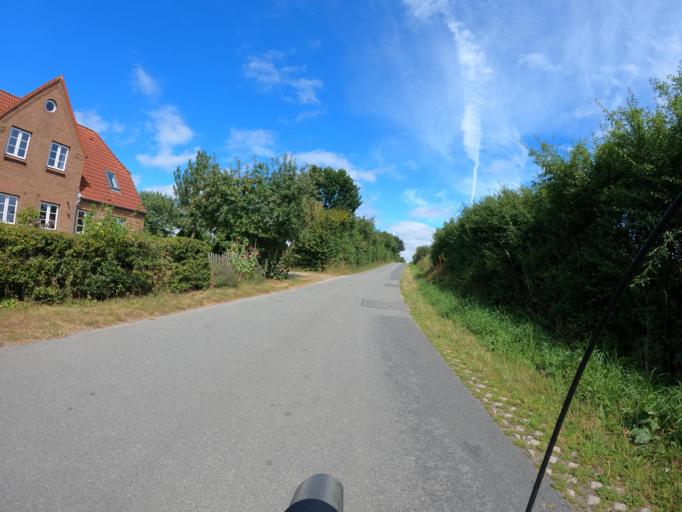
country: DE
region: Schleswig-Holstein
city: Steinbergkirche
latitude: 54.7948
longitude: 9.7440
